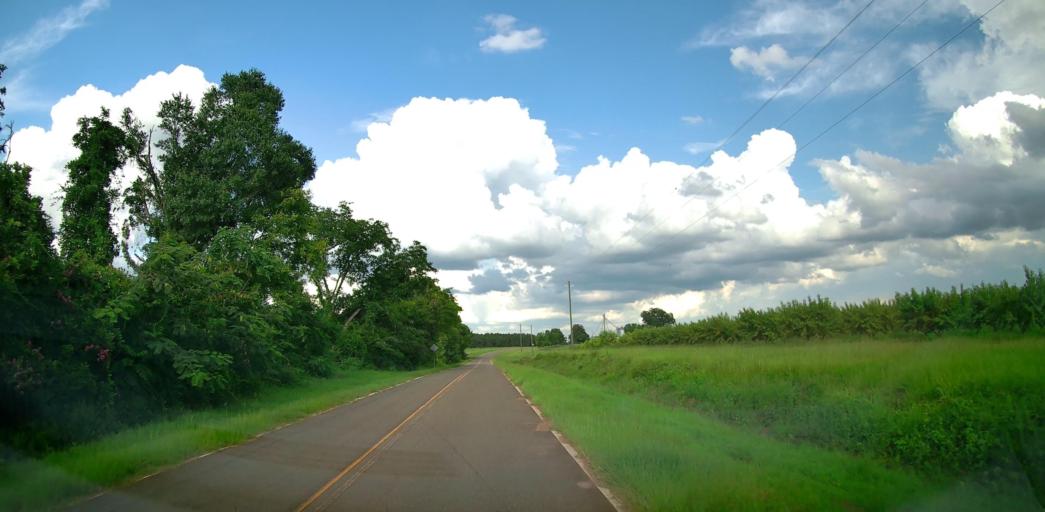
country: US
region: Georgia
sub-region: Bleckley County
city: Cochran
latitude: 32.4132
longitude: -83.4522
